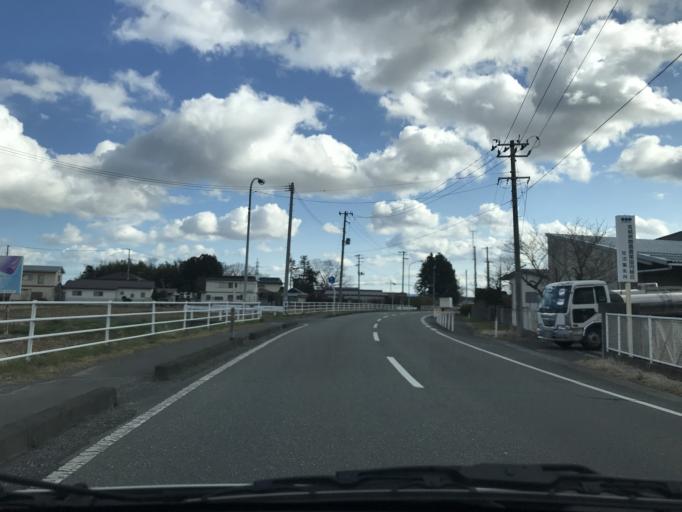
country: JP
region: Miyagi
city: Wakuya
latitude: 38.6694
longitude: 141.1944
